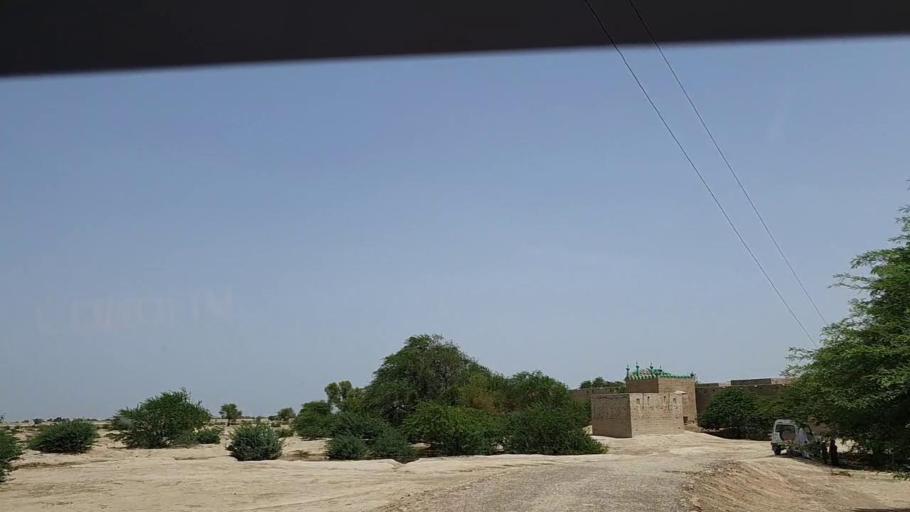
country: PK
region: Sindh
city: Johi
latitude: 26.7140
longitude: 67.6531
